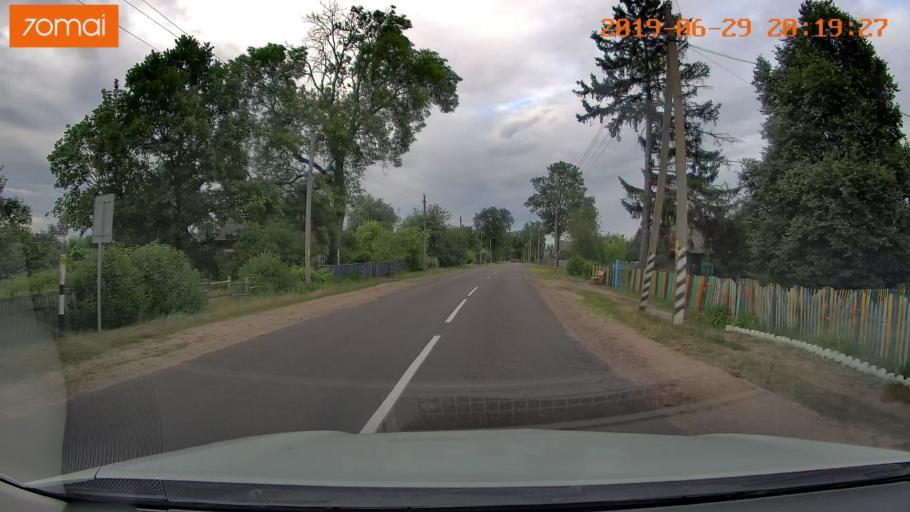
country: BY
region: Brest
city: Asnyezhytsy
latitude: 52.4014
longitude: 26.2442
